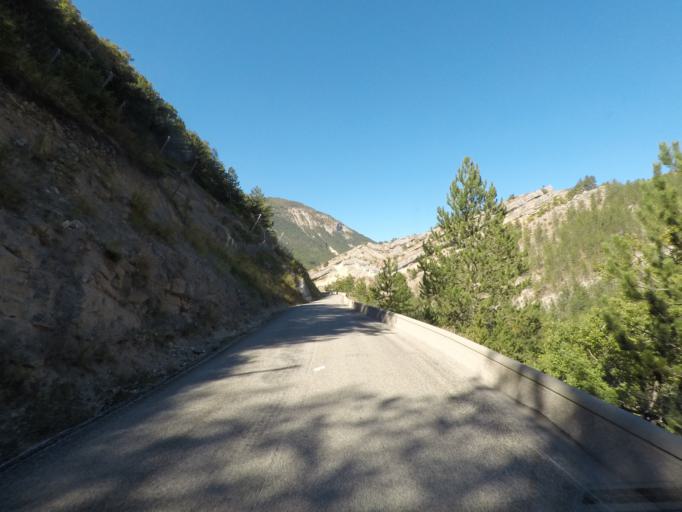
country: FR
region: Rhone-Alpes
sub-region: Departement de la Drome
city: Die
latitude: 44.6599
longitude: 5.2822
